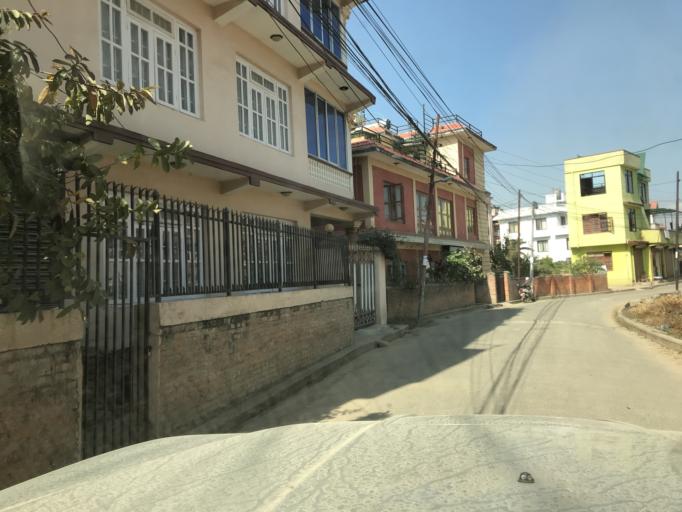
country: NP
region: Central Region
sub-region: Bagmati Zone
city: Patan
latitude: 27.6451
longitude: 85.3174
